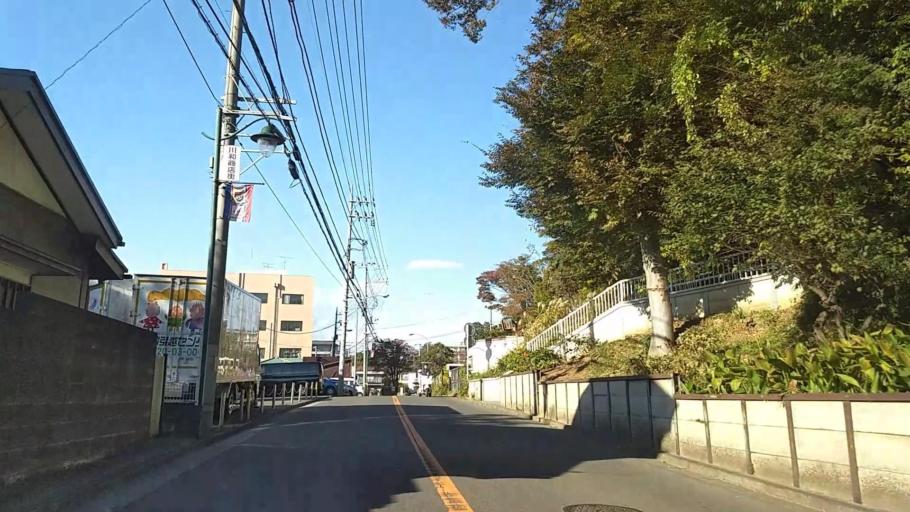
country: JP
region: Tokyo
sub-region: Machida-shi
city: Machida
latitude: 35.5216
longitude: 139.5534
